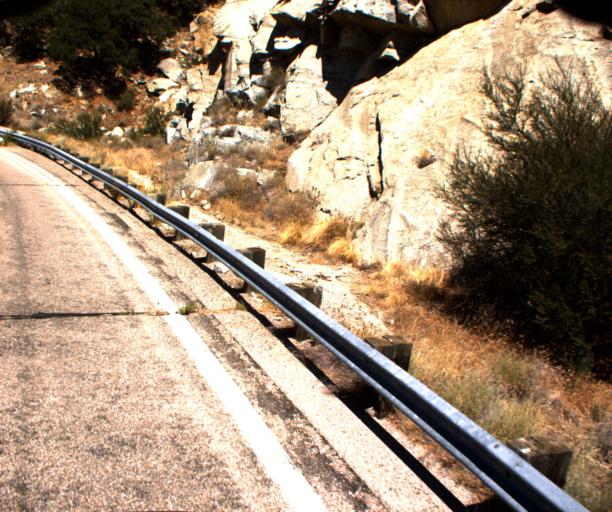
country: US
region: Arizona
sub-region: Pima County
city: Sells
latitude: 31.9634
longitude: -111.6216
